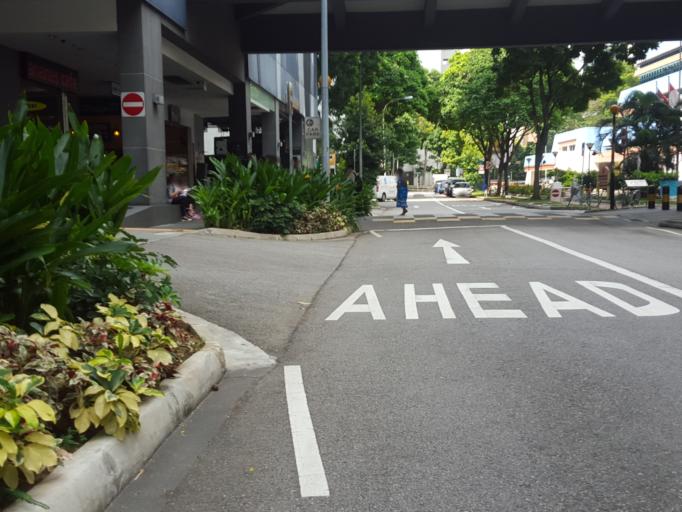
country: SG
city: Singapore
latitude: 1.3082
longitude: 103.8625
